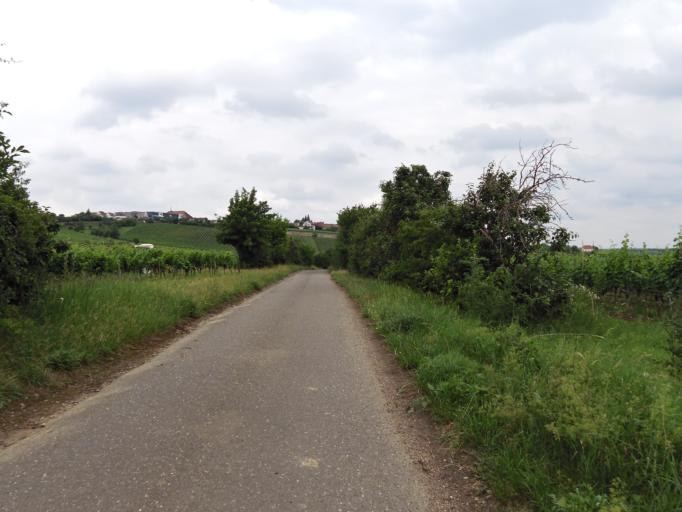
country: DE
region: Rheinland-Pfalz
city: Herxheim am Berg
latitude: 49.5032
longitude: 8.1837
